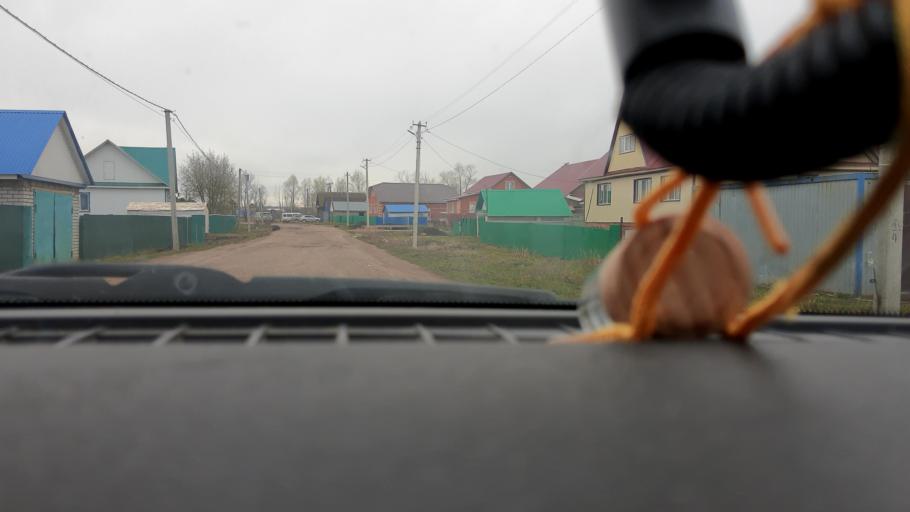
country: RU
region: Bashkortostan
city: Asanovo
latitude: 54.8167
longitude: 55.5640
